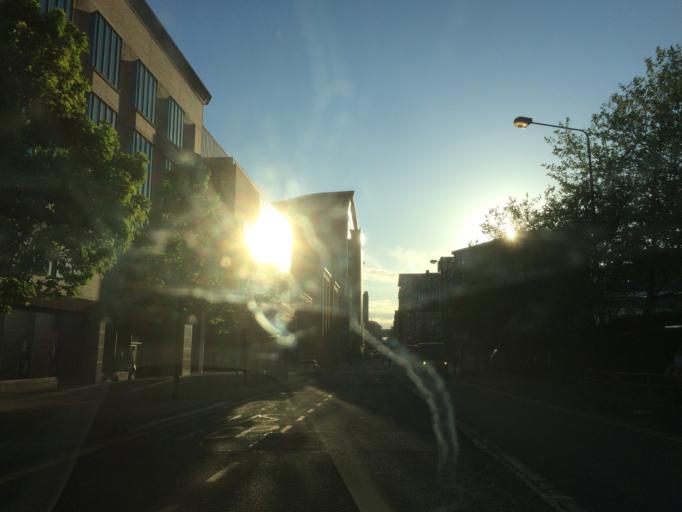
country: GB
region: Scotland
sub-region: Glasgow City
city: Glasgow
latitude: 55.8647
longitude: -4.2508
